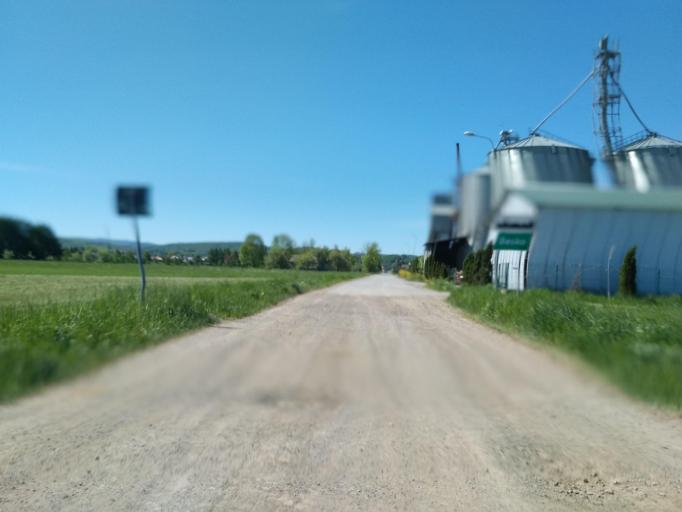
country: PL
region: Subcarpathian Voivodeship
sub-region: Powiat sanocki
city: Besko
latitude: 49.6008
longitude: 21.9709
